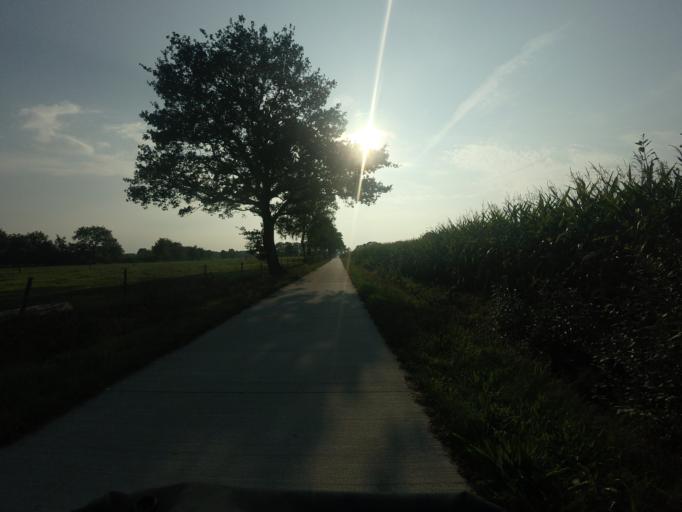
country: NL
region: Drenthe
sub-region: Gemeente Tynaarlo
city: Vries
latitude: 53.1259
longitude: 6.5497
